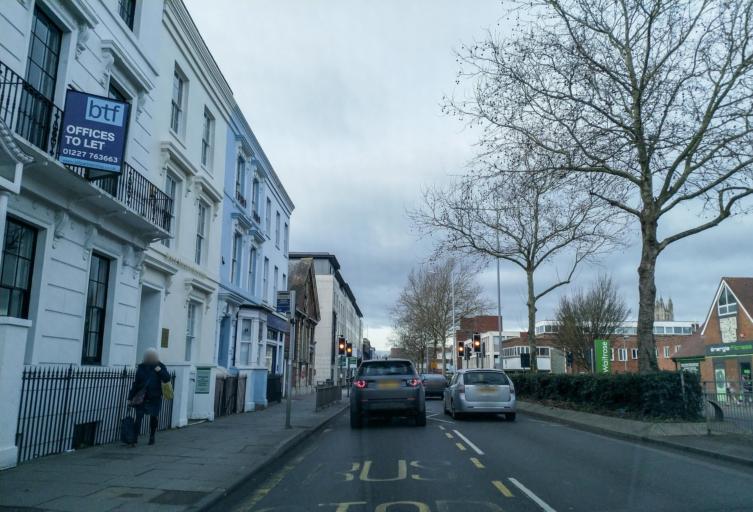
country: GB
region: England
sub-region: Kent
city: Canterbury
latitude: 51.2758
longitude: 1.0861
